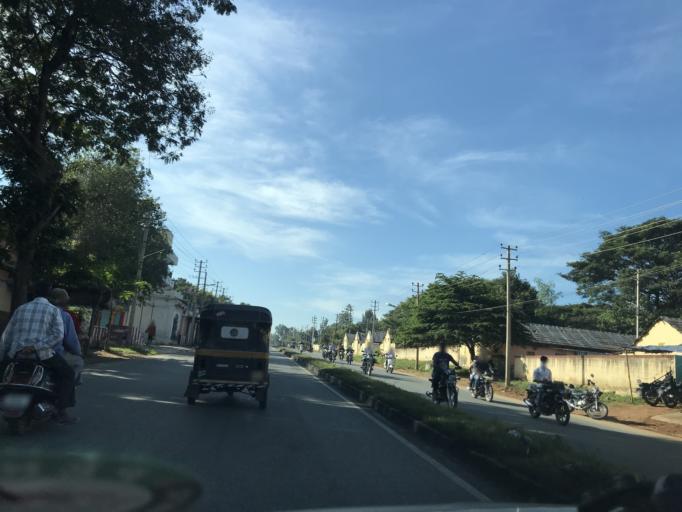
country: IN
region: Karnataka
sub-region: Mysore
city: Mysore
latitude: 12.2782
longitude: 76.6399
